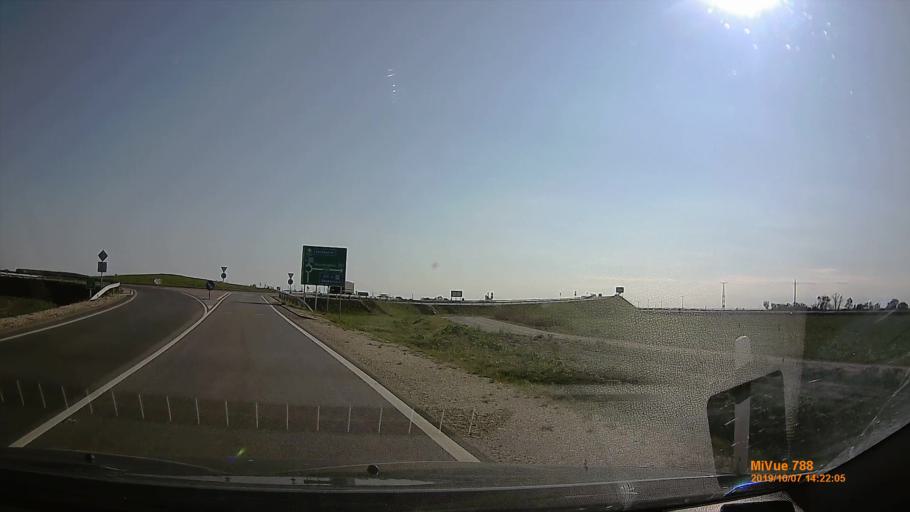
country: HU
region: Jasz-Nagykun-Szolnok
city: Kunszentmarton
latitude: 46.8748
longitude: 20.2659
